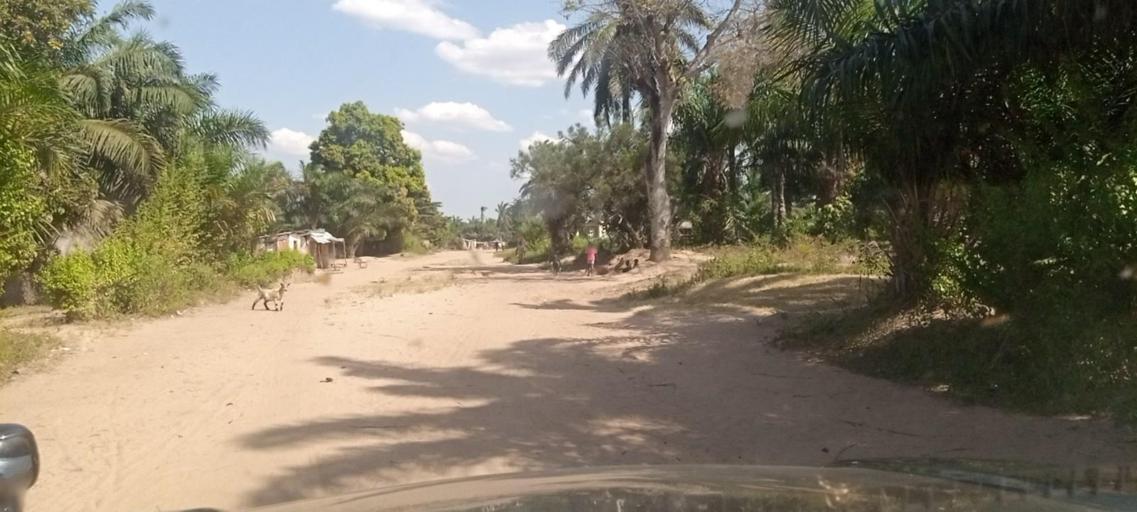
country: CD
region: Kasai-Oriental
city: Kabinda
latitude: -6.1279
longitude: 24.5266
